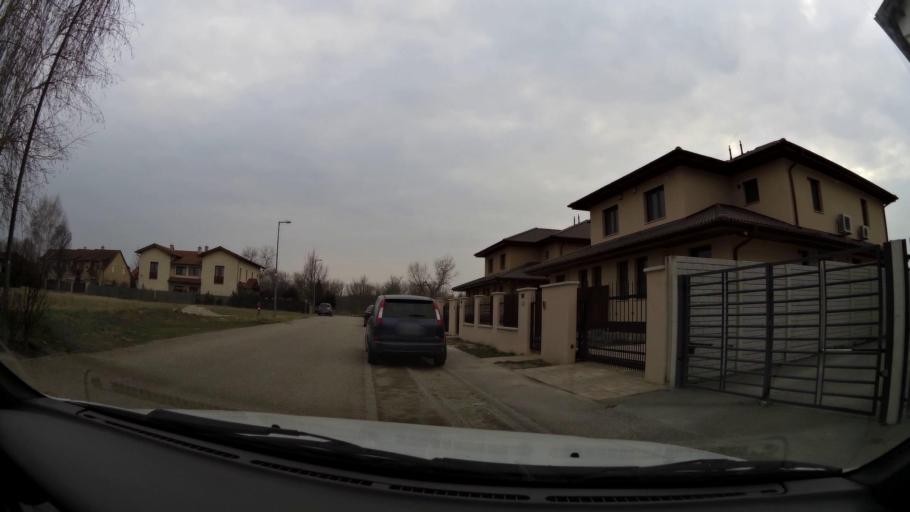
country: HU
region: Budapest
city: Budapest XVII. keruelet
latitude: 47.4709
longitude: 19.2207
